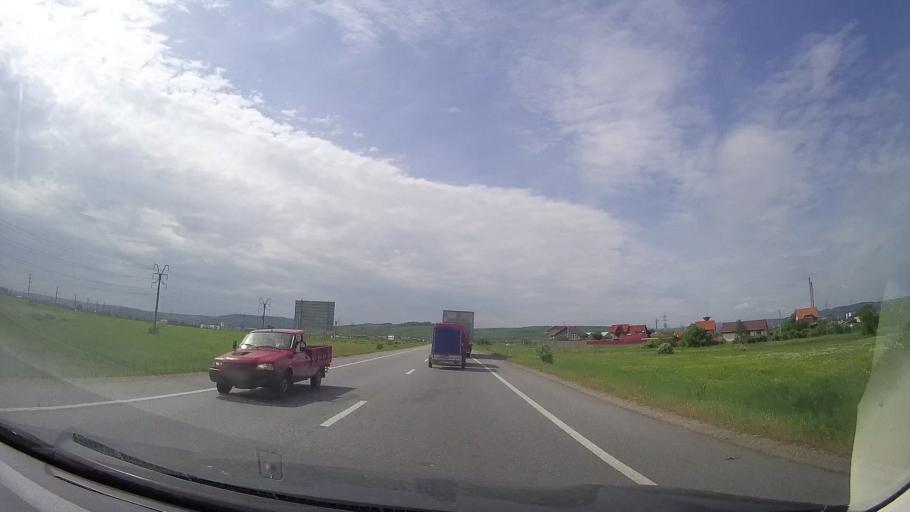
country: RO
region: Mehedinti
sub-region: Comuna Simian
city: Dudasu
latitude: 44.6498
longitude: 22.6915
